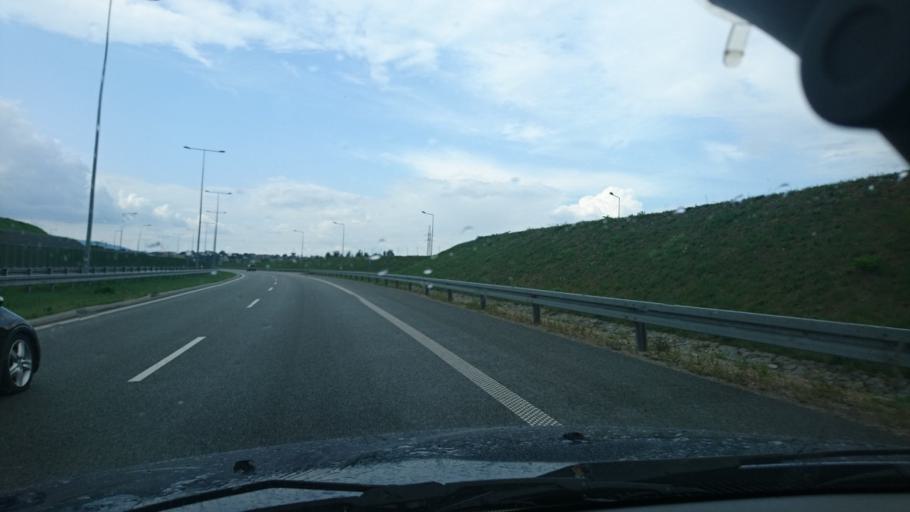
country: PL
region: Silesian Voivodeship
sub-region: Powiat zywiecki
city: Pietrzykowice
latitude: 49.6822
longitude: 19.1671
